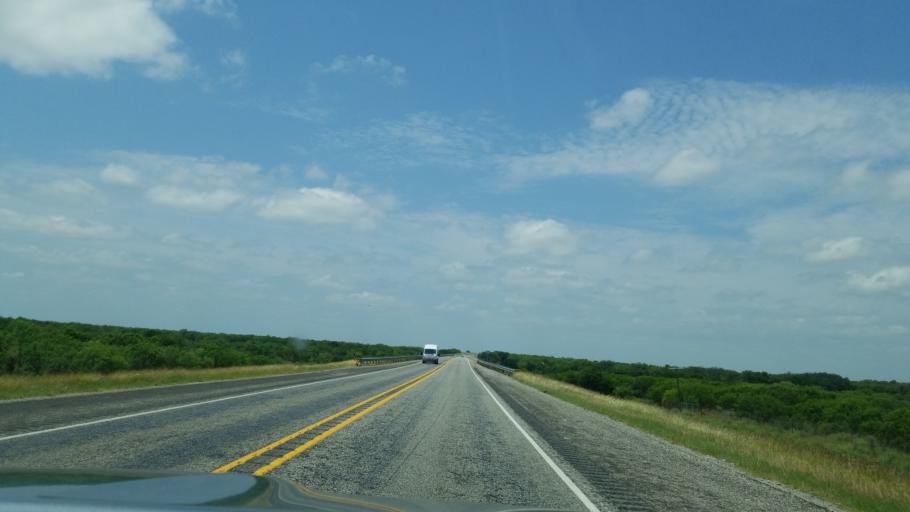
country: US
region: Texas
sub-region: Zavala County
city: La Pryor
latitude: 28.9347
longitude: -99.7914
